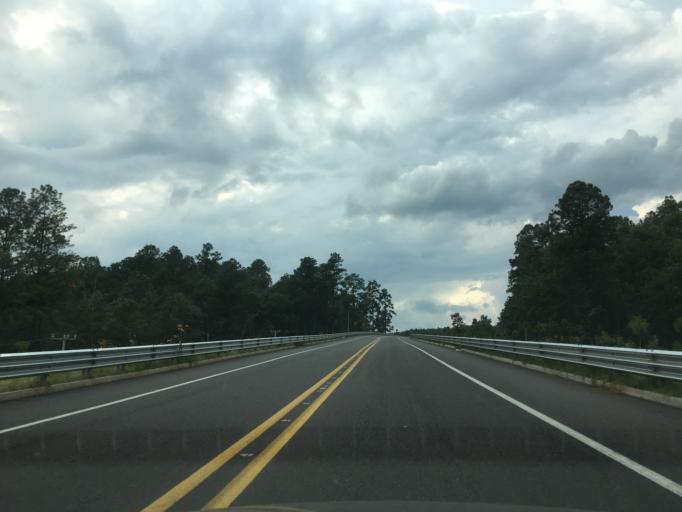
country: MX
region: Michoacan
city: Angahuan
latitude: 19.5165
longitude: -102.1741
